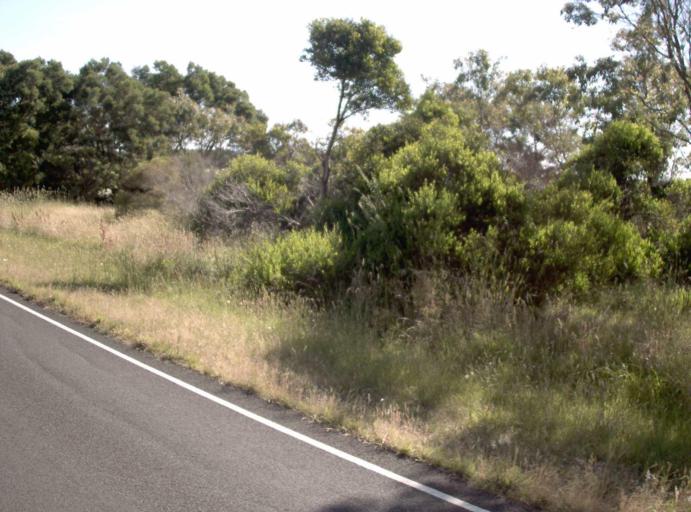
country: AU
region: Victoria
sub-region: Latrobe
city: Traralgon
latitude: -38.6322
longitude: 146.6760
